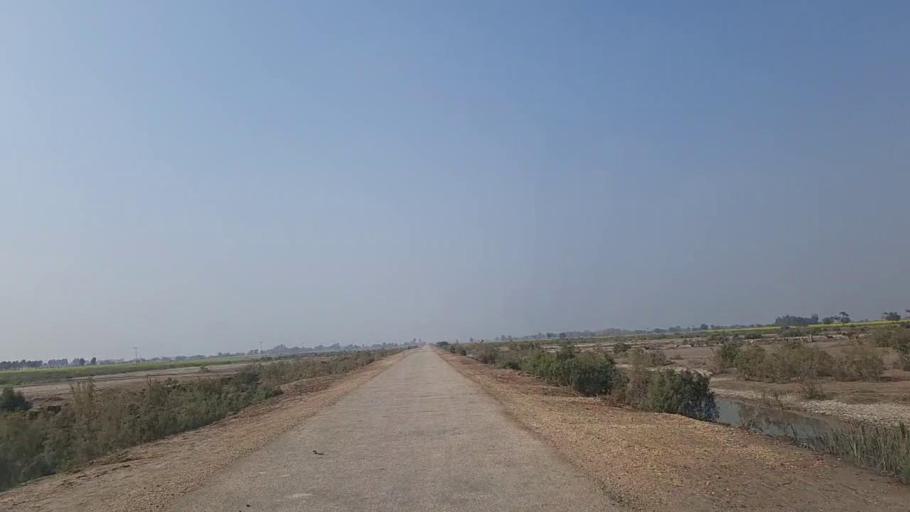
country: PK
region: Sindh
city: Nawabshah
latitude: 26.3598
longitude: 68.4363
